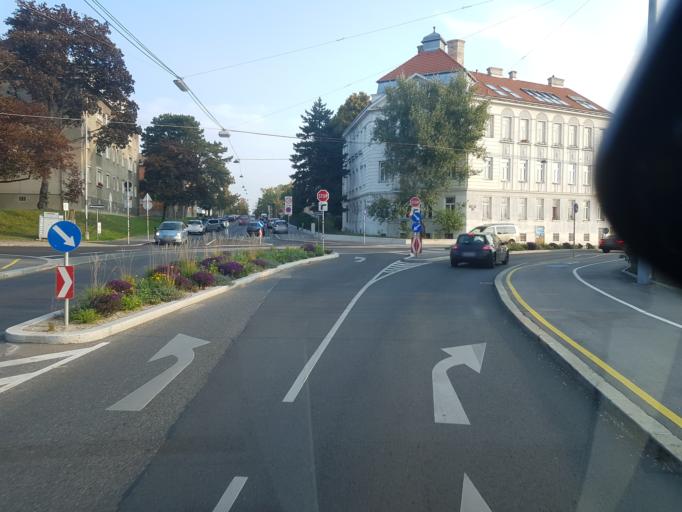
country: AT
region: Vienna
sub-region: Wien Stadt
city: Vienna
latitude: 48.2264
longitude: 16.3243
